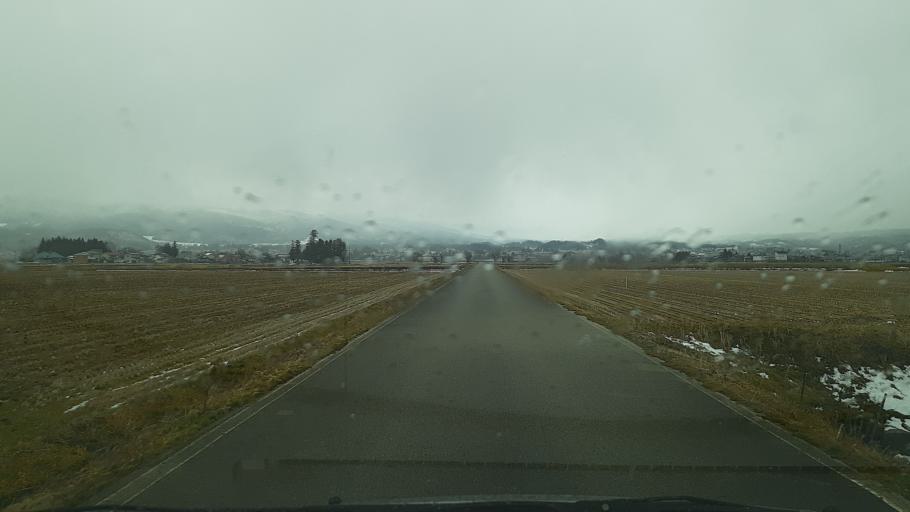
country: JP
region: Fukushima
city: Kitakata
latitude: 37.5589
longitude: 139.8972
